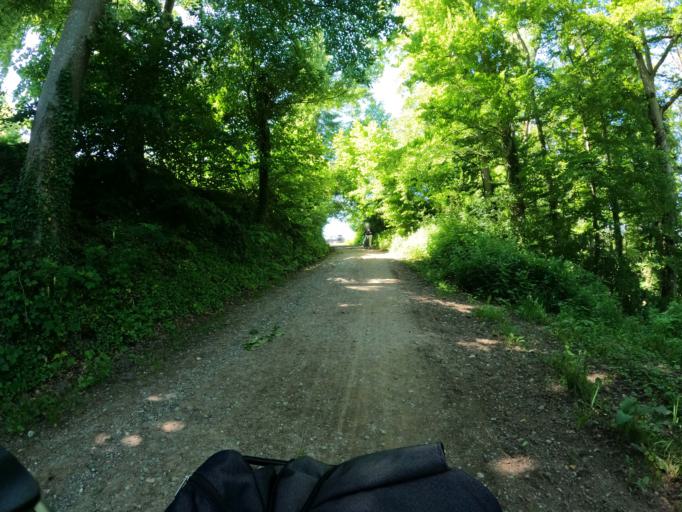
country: CH
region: Zurich
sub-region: Bezirk Affoltern
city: Affoltern / Sonnenberg
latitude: 47.2834
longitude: 8.4795
